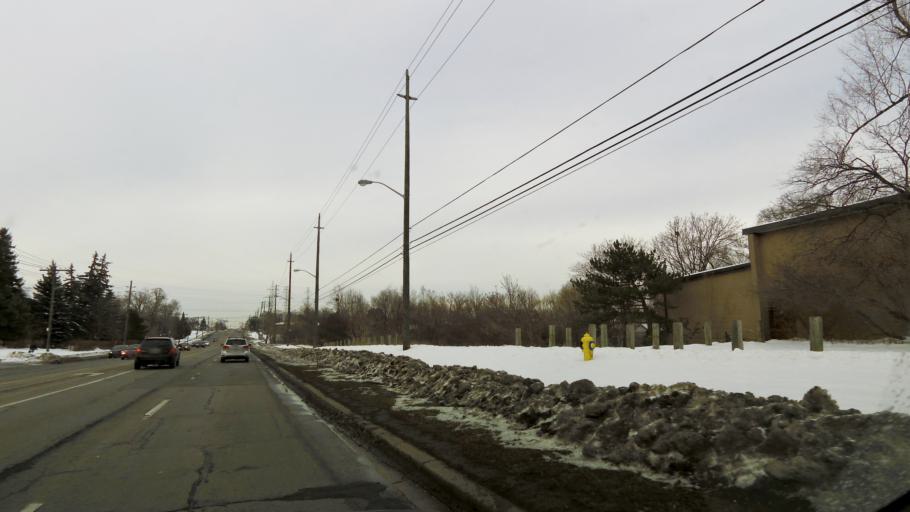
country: CA
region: Ontario
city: Etobicoke
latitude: 43.7188
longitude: -79.5568
